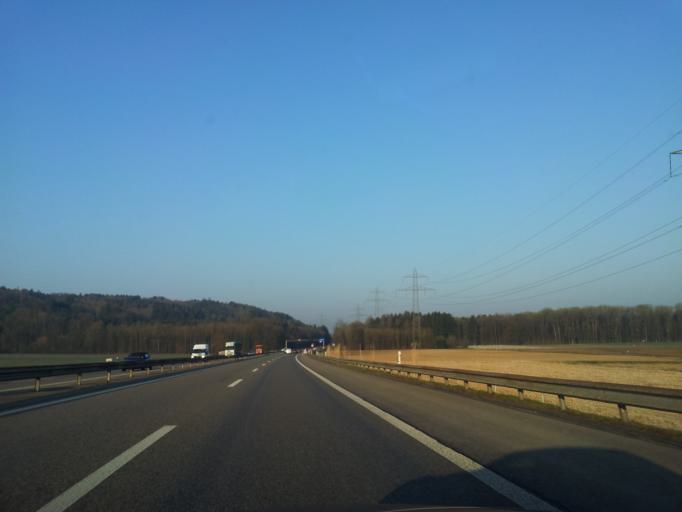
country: CH
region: Aargau
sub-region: Bezirk Rheinfelden
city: Magden
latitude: 47.5462
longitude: 7.8242
